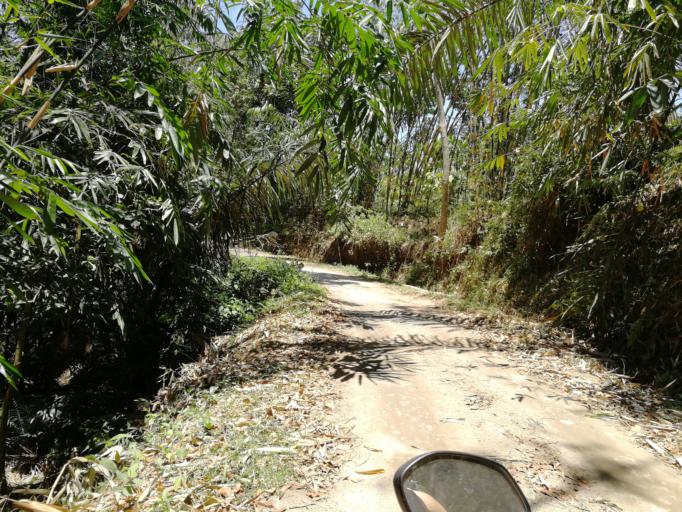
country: ID
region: West Nusa Tenggara
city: Tetebatu
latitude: -8.5456
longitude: 116.4202
